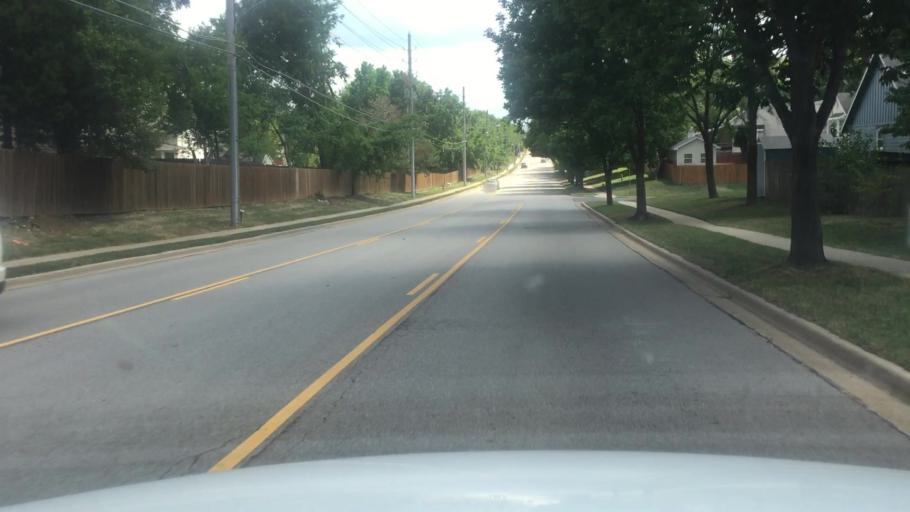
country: US
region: Kansas
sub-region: Johnson County
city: Lenexa
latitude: 38.9624
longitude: -94.7610
